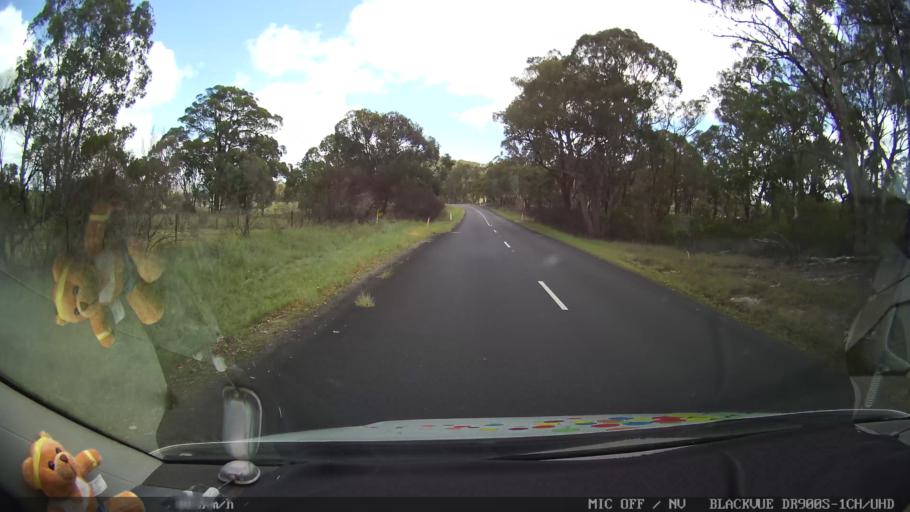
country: AU
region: New South Wales
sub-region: Glen Innes Severn
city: Glen Innes
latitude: -29.5399
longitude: 151.6717
